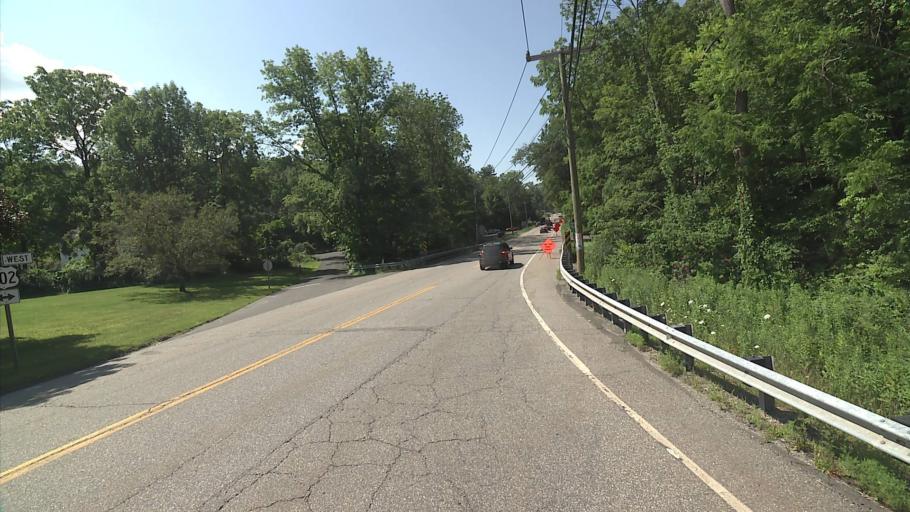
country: US
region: Connecticut
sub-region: Litchfield County
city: New Preston
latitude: 41.6744
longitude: -73.3546
